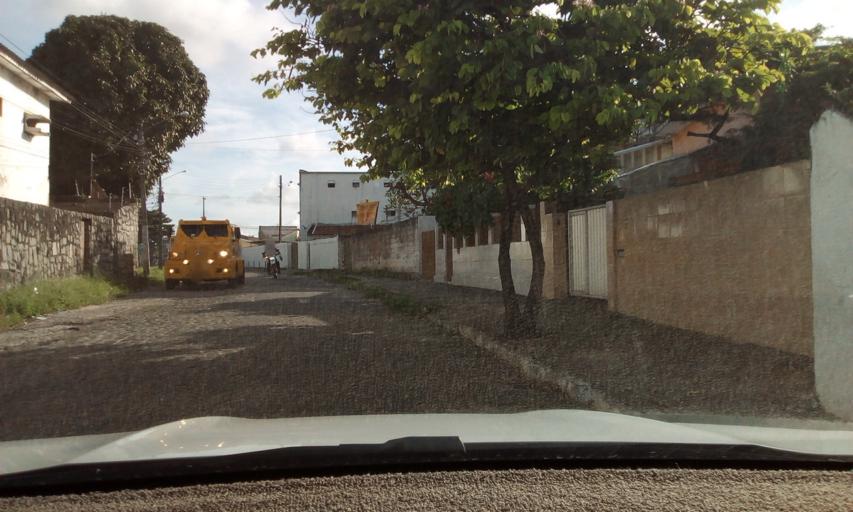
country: BR
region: Paraiba
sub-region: Joao Pessoa
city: Joao Pessoa
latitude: -7.1365
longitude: -34.8876
